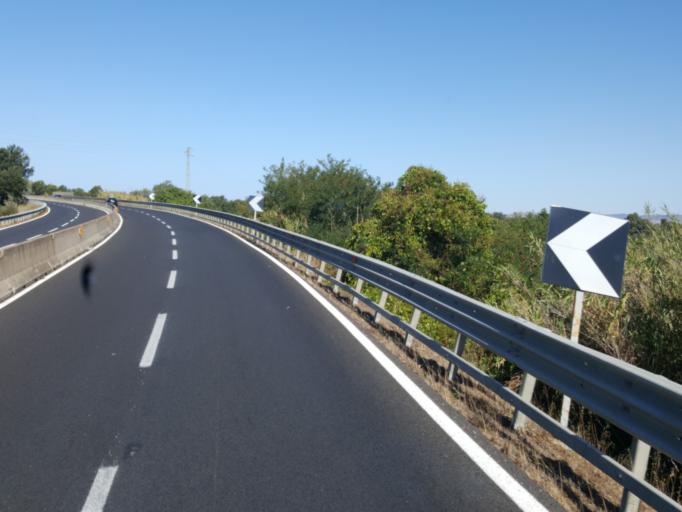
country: IT
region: Tuscany
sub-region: Provincia di Grosseto
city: Albinia
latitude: 42.4777
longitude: 11.2306
